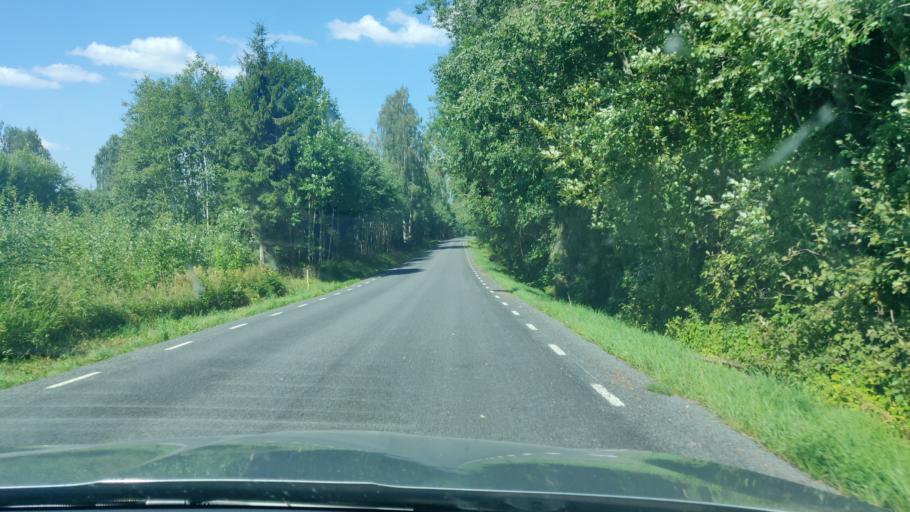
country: EE
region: Tartu
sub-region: Elva linn
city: Elva
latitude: 58.1529
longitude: 26.4718
